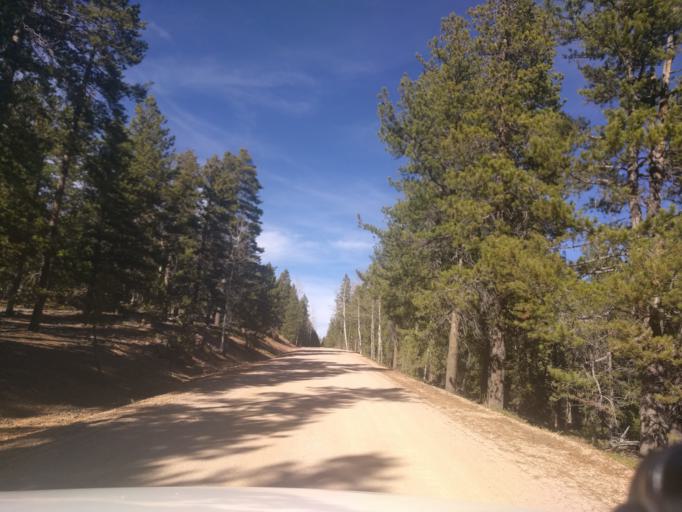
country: US
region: Colorado
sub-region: Douglas County
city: Perry Park
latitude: 39.1952
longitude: -105.0519
